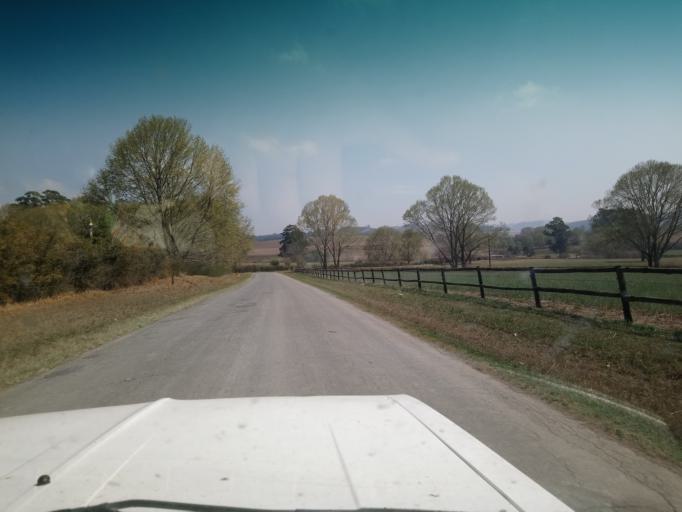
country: ZA
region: KwaZulu-Natal
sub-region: uMgungundlovu District Municipality
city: Howick
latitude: -29.3815
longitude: 30.2328
